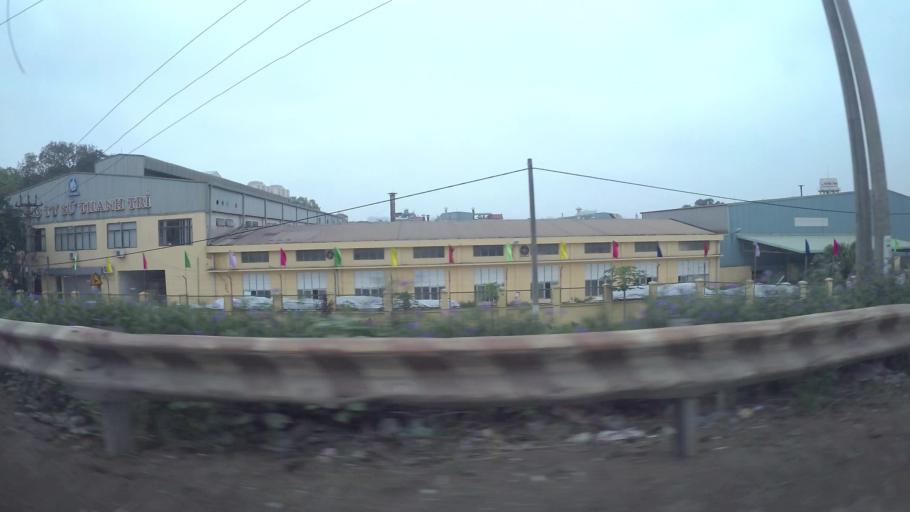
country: VN
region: Ha Noi
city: Hai BaTrung
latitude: 20.9955
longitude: 105.8925
